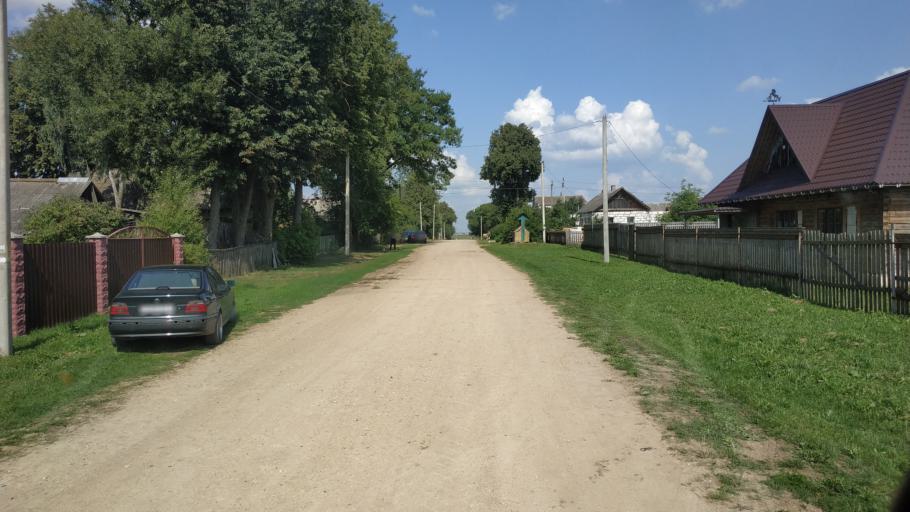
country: BY
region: Mogilev
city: Buynichy
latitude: 53.9659
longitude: 30.1944
